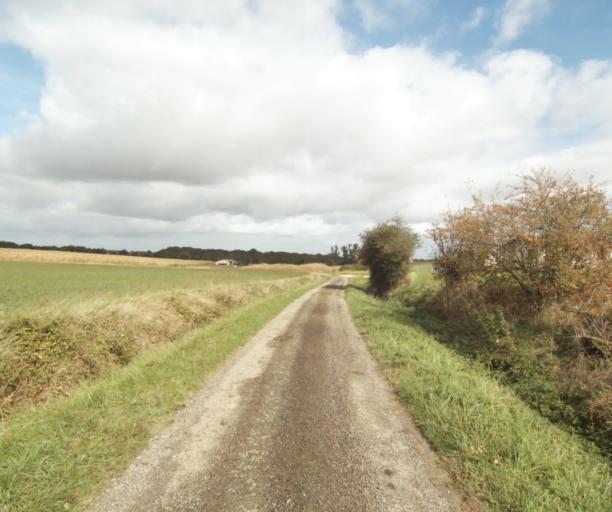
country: FR
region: Midi-Pyrenees
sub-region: Departement du Tarn-et-Garonne
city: Beaumont-de-Lomagne
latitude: 43.8667
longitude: 1.0791
